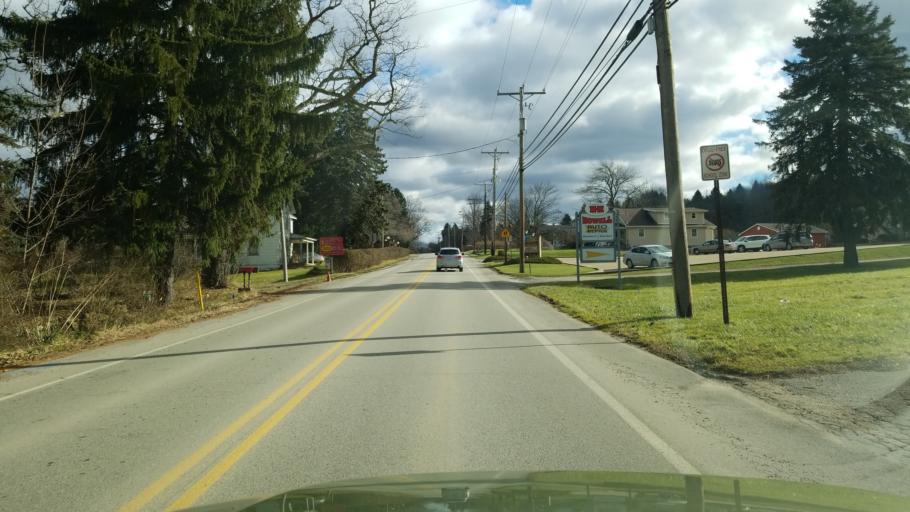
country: US
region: Pennsylvania
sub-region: Indiana County
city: Chevy Chase Heights
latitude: 40.6204
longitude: -79.1300
